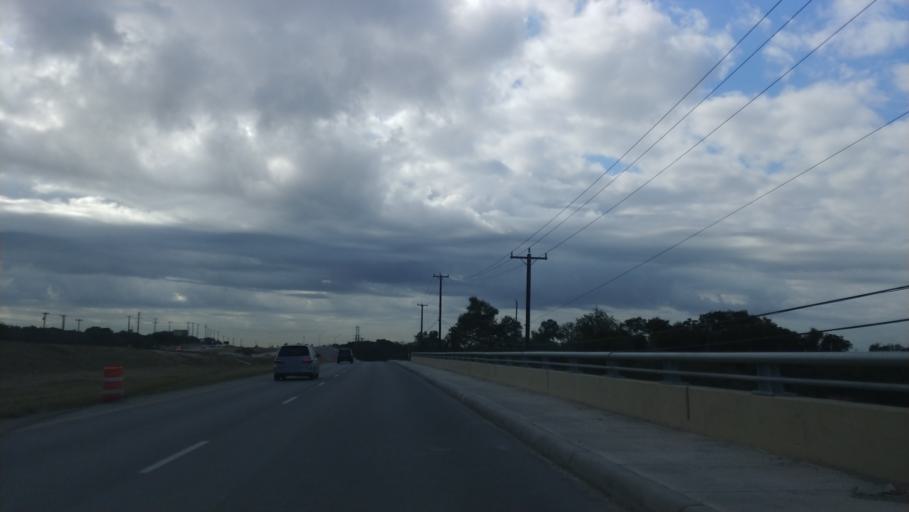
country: US
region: Texas
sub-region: Bexar County
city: Leon Valley
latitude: 29.4636
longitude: -98.7121
